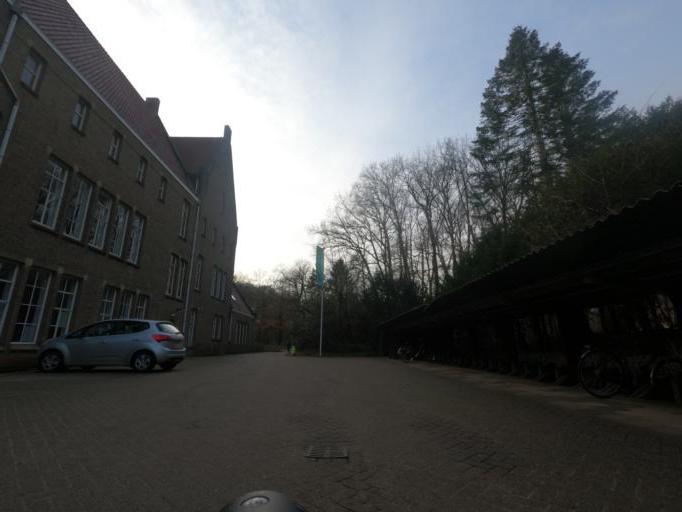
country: NL
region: Utrecht
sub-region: Gemeente Amersfoort
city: Amersfoort
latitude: 52.1458
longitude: 5.3520
